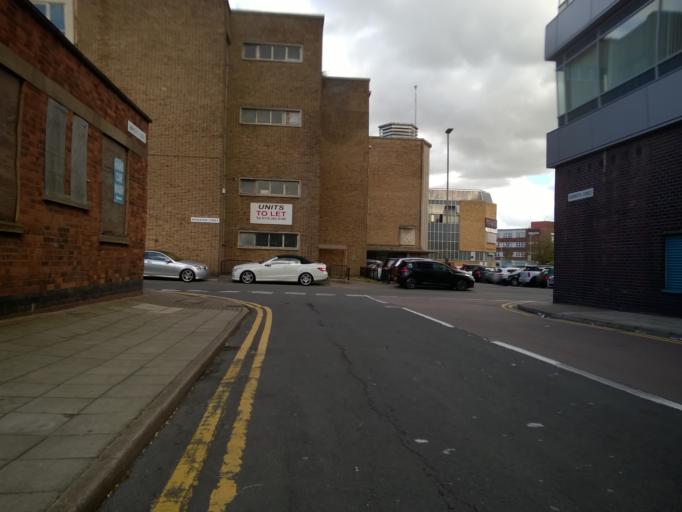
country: GB
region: England
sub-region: City of Leicester
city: Leicester
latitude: 52.6418
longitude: -1.1312
